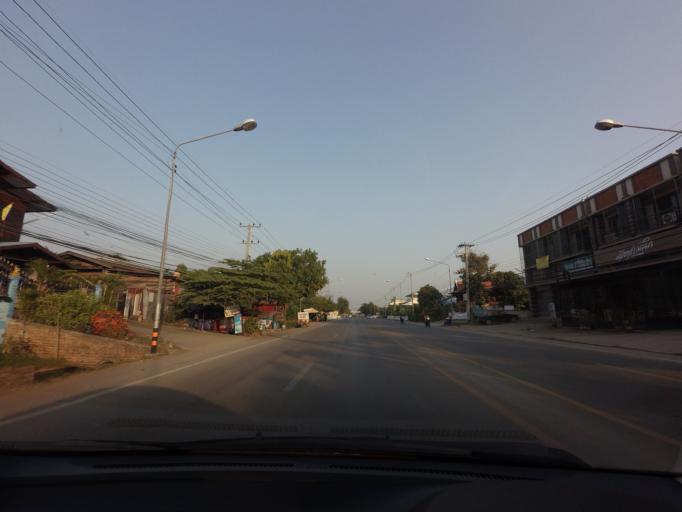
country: TH
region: Sukhothai
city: Sukhothai
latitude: 17.0107
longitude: 99.7864
